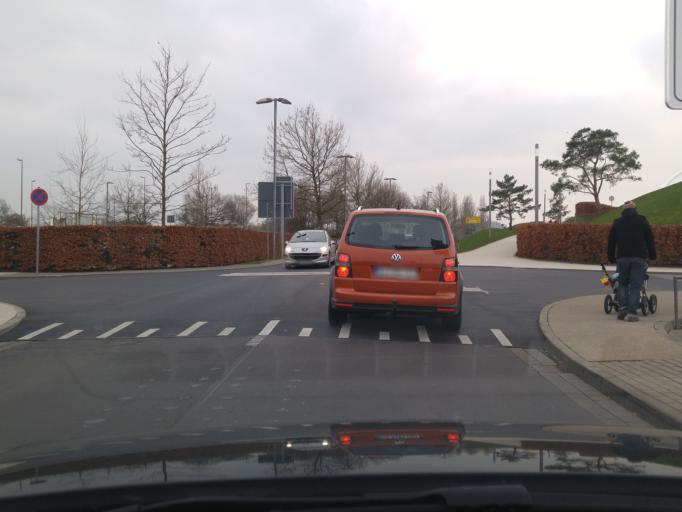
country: DE
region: Lower Saxony
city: Wolfsburg
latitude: 52.4342
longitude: 10.7983
